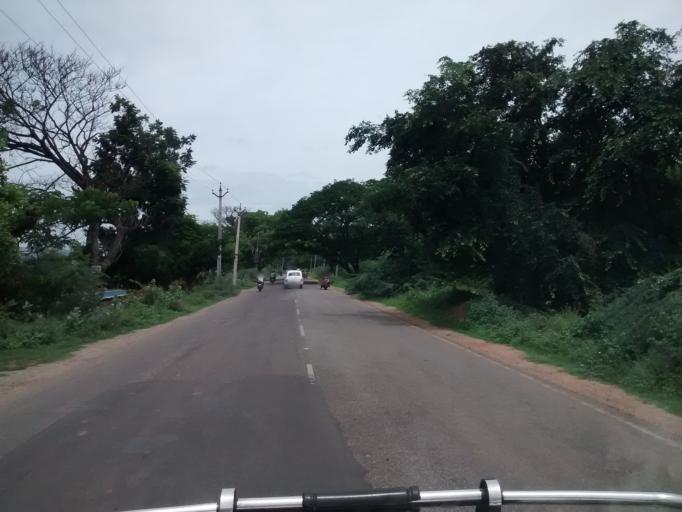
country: IN
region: Andhra Pradesh
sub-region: Chittoor
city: Narasingapuram
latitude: 13.6127
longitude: 79.3581
